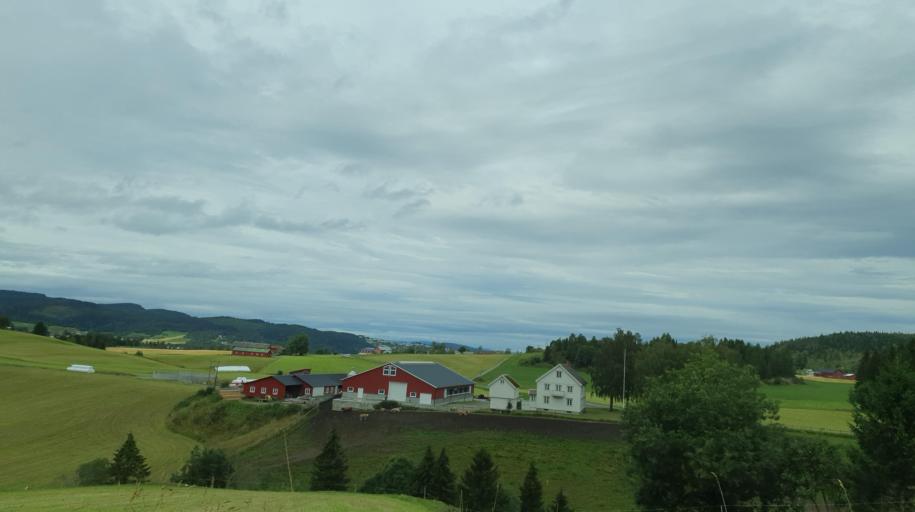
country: NO
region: Nord-Trondelag
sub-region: Stjordal
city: Stjordalshalsen
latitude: 63.4110
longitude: 10.9705
